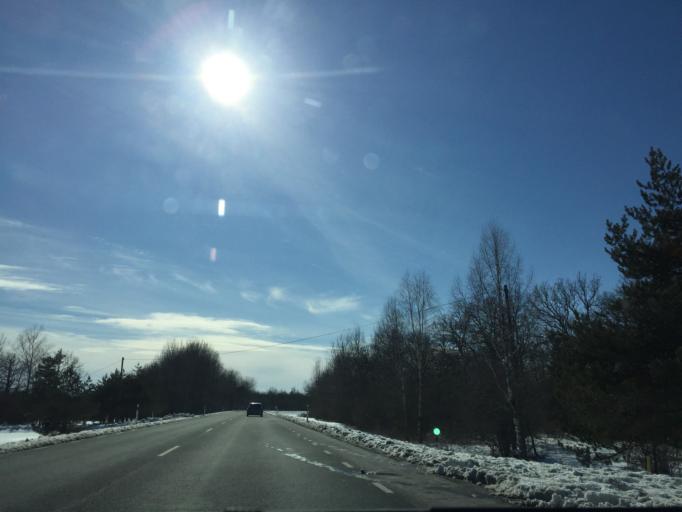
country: EE
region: Saare
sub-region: Kuressaare linn
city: Kuressaare
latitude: 58.3182
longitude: 22.6260
